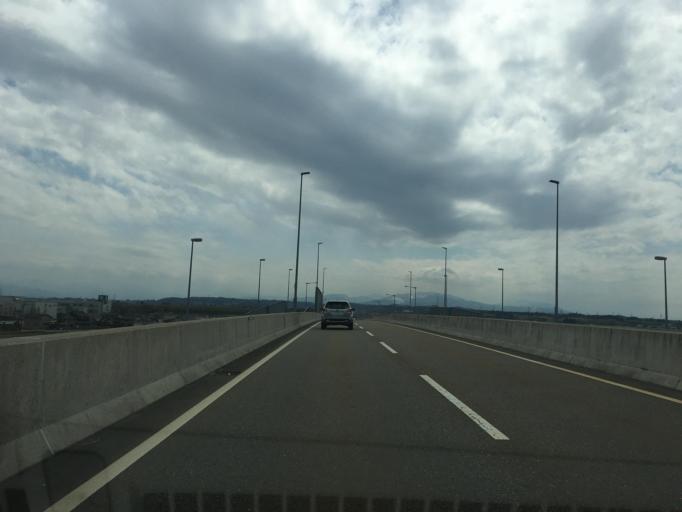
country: JP
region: Toyama
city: Kuragaki-kosugi
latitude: 36.7175
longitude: 137.1187
